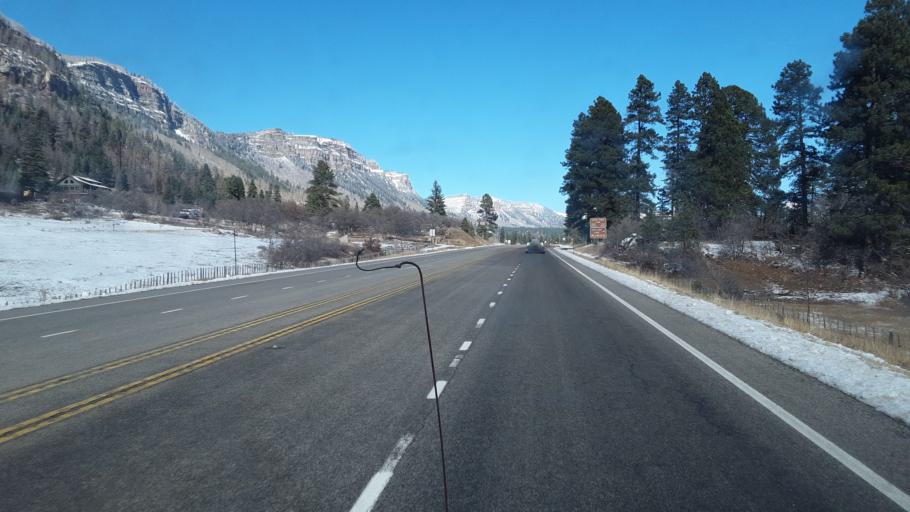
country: US
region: Colorado
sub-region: La Plata County
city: Durango
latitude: 37.5256
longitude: -107.8178
